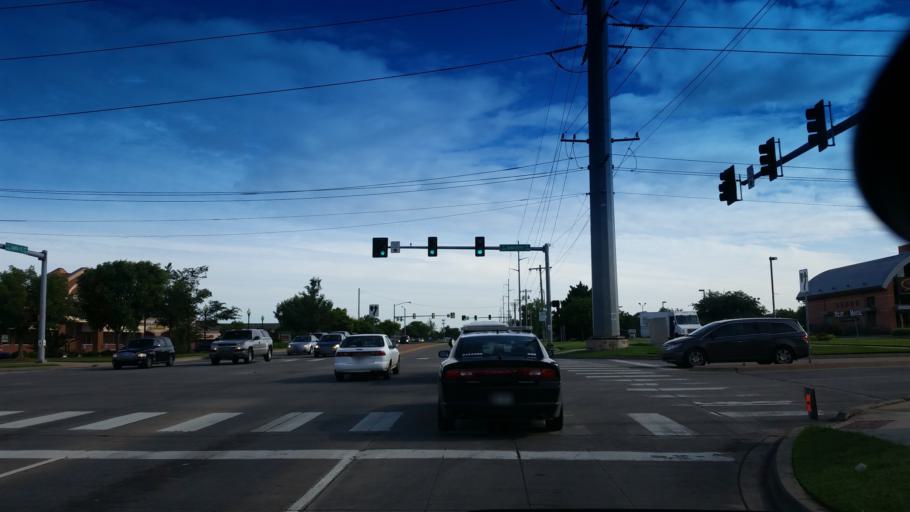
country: US
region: Oklahoma
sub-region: Oklahoma County
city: Edmond
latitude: 35.6673
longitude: -97.5140
